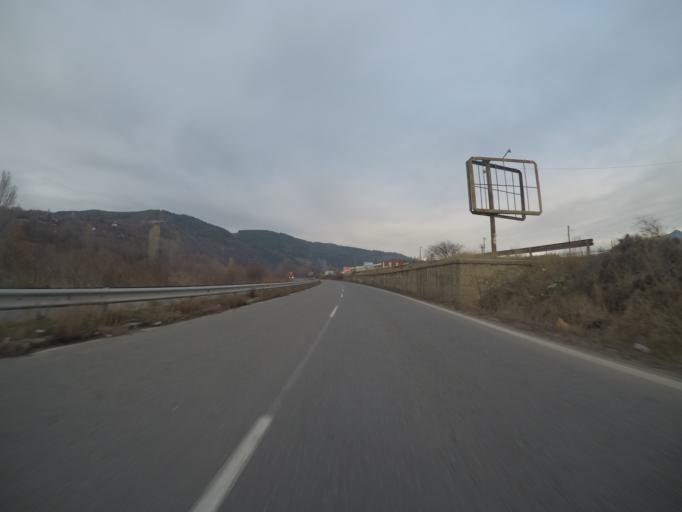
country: BG
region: Kyustendil
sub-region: Obshtina Dupnitsa
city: Dupnitsa
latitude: 42.2617
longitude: 23.1017
